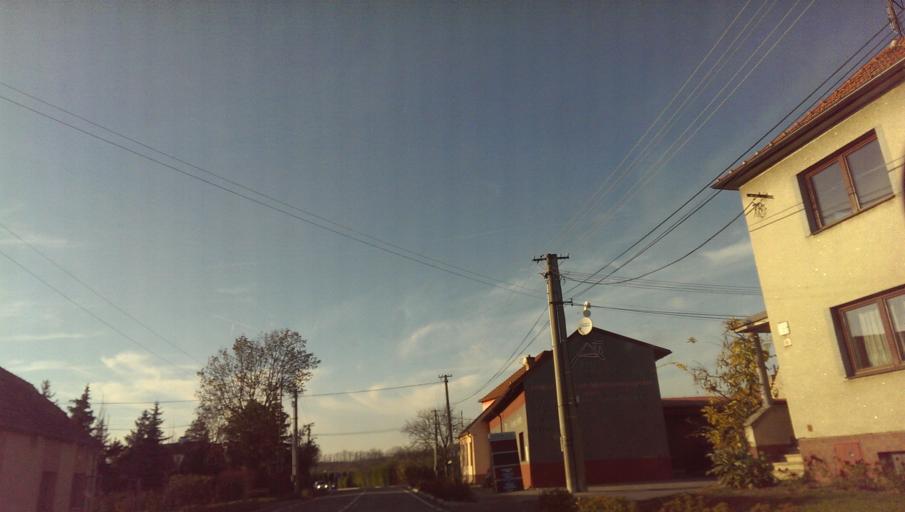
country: CZ
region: South Moravian
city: Louka
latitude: 48.9164
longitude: 17.4848
